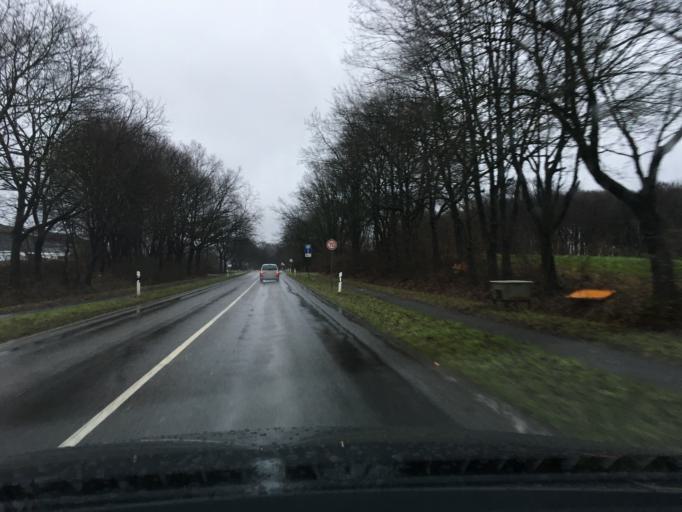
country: DE
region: North Rhine-Westphalia
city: Wulfrath
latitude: 51.2922
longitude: 7.0968
